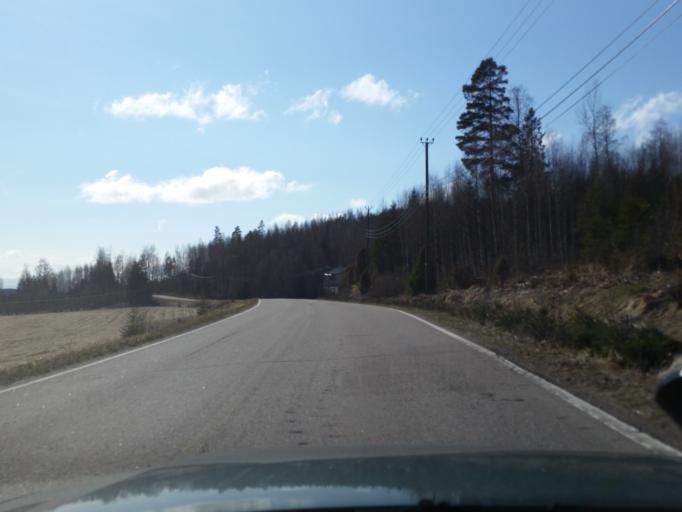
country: FI
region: Uusimaa
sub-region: Helsinki
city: Kaerkoelae
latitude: 60.5161
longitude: 23.9992
